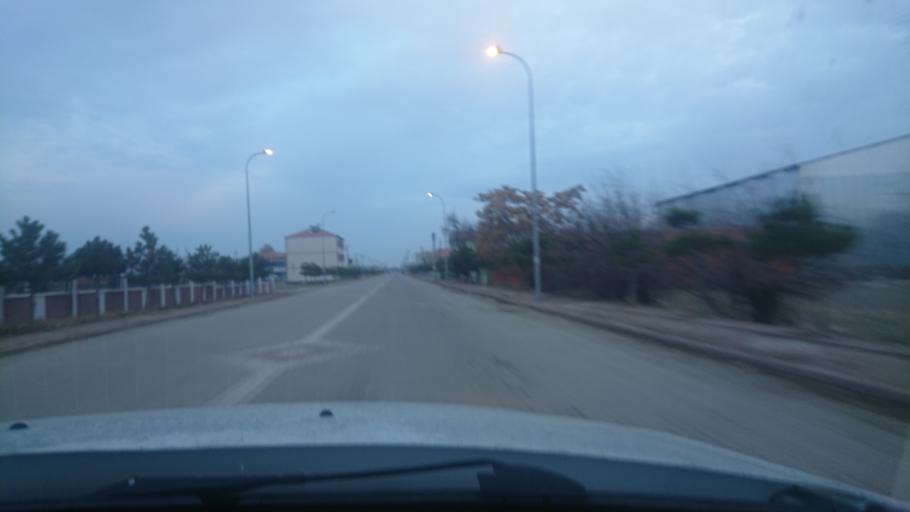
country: TR
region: Aksaray
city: Yesilova
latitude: 38.3338
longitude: 33.7517
